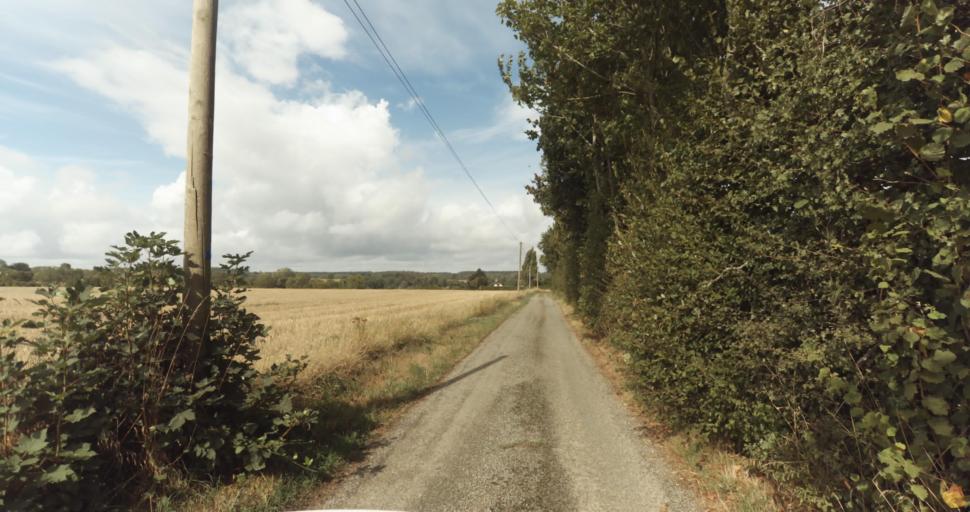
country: FR
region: Lower Normandy
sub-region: Departement de l'Orne
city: Gace
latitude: 48.8241
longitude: 0.3805
